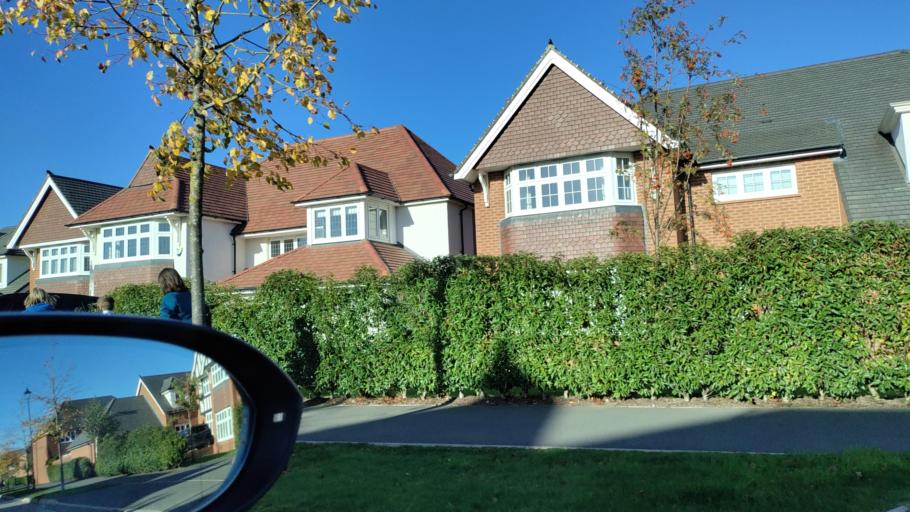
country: GB
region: England
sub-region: Cheshire West and Chester
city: Hartford
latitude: 53.2467
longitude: -2.5518
